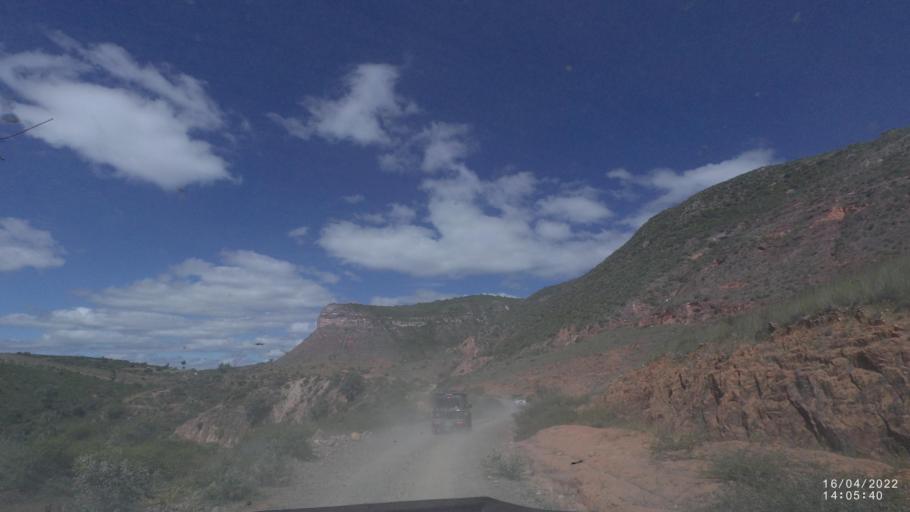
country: BO
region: Cochabamba
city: Mizque
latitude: -18.0568
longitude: -65.5356
